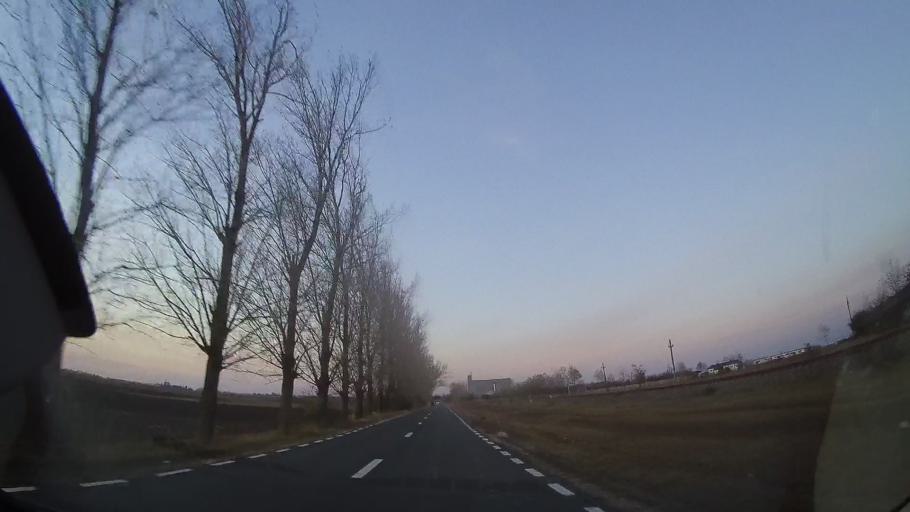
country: RO
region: Constanta
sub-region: Comuna Cobadin
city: Cobadin
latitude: 44.0459
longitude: 28.2526
